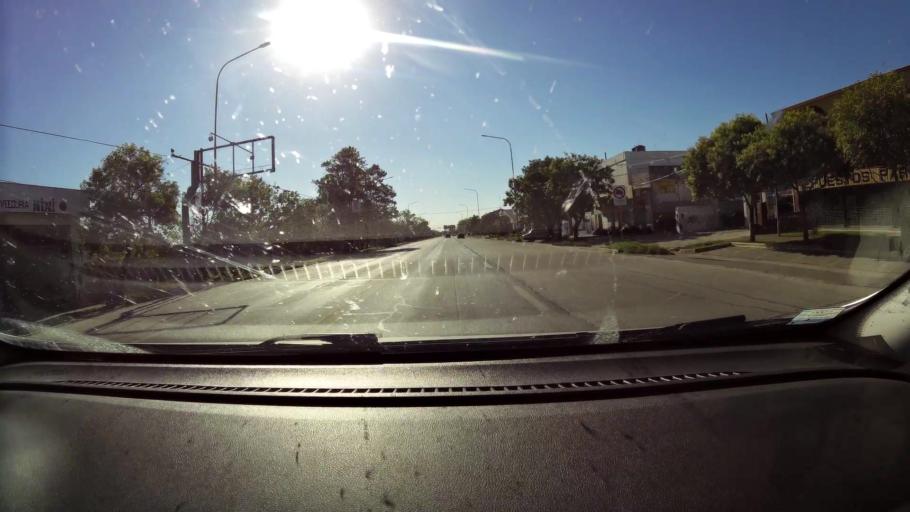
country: AR
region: Cordoba
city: San Francisco
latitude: -31.4162
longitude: -62.0856
